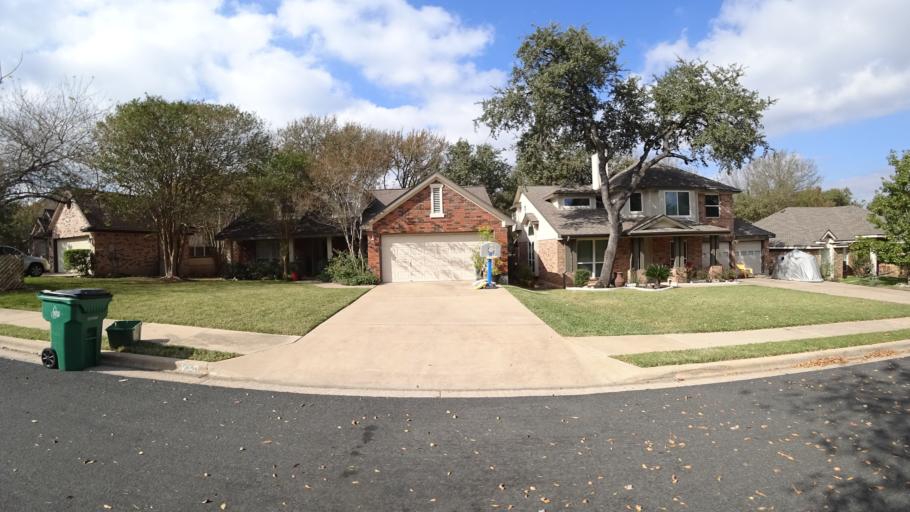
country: US
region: Texas
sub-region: Travis County
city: Shady Hollow
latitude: 30.1618
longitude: -97.8511
